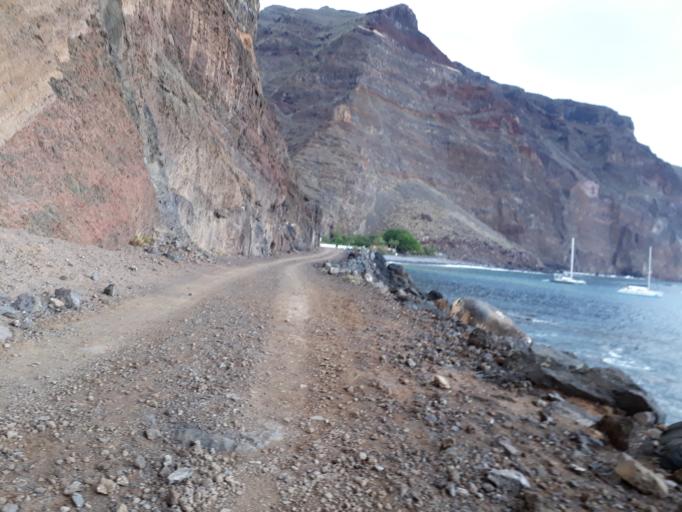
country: ES
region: Canary Islands
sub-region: Provincia de Santa Cruz de Tenerife
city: Alajero
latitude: 28.0804
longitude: -17.3272
